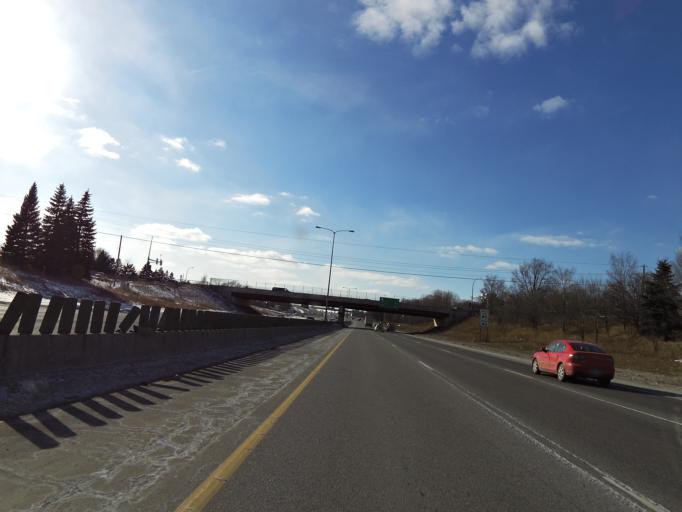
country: US
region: Minnesota
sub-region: Dakota County
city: South Saint Paul
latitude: 44.8745
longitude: -93.0406
